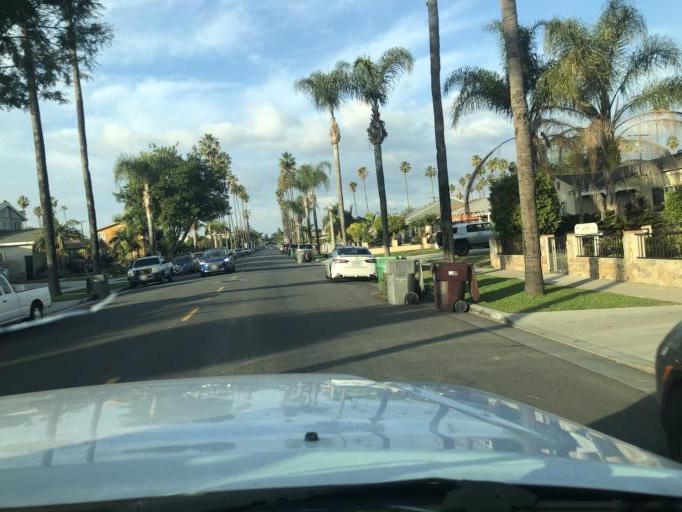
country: US
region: California
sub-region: Orange County
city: Santa Ana
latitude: 33.7208
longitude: -117.8700
